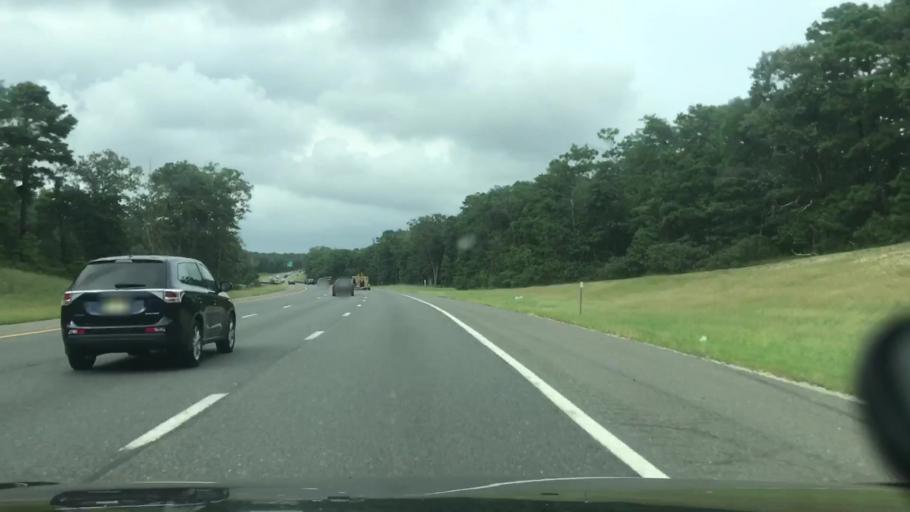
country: US
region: New Jersey
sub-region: Ocean County
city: Barnegat
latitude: 39.7776
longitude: -74.2434
